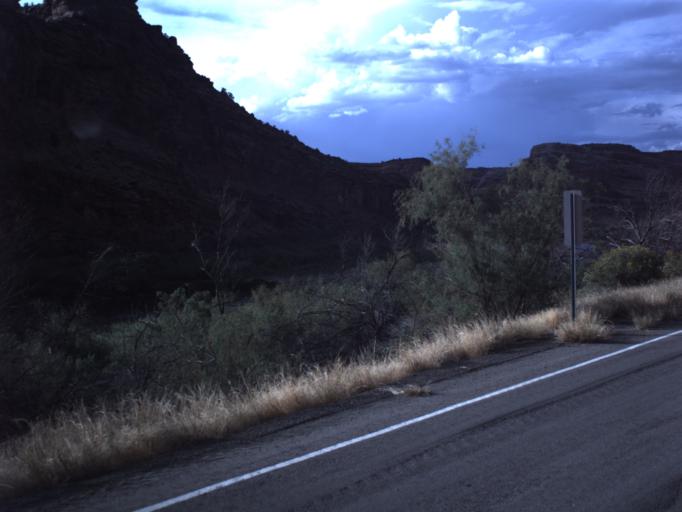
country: US
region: Utah
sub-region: Grand County
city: Moab
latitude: 38.7995
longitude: -109.3121
